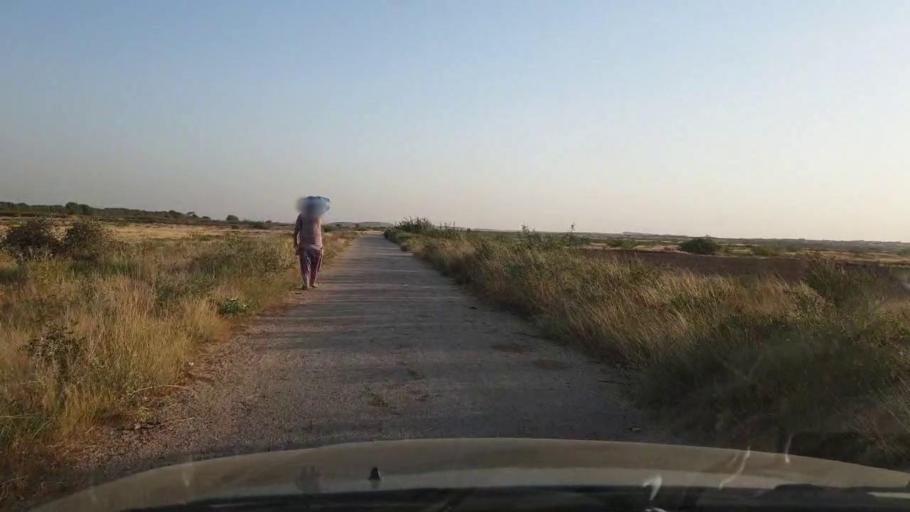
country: PK
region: Sindh
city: Kotri
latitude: 25.2286
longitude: 68.2245
